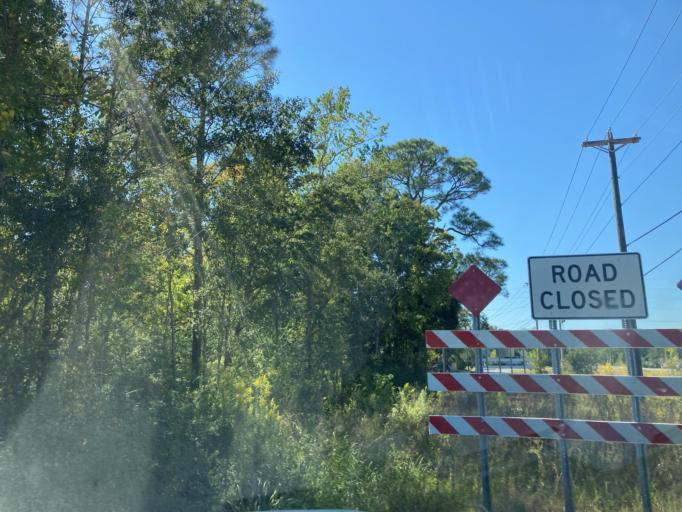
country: US
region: Mississippi
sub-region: Jackson County
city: Saint Martin
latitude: 30.4576
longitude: -88.8648
